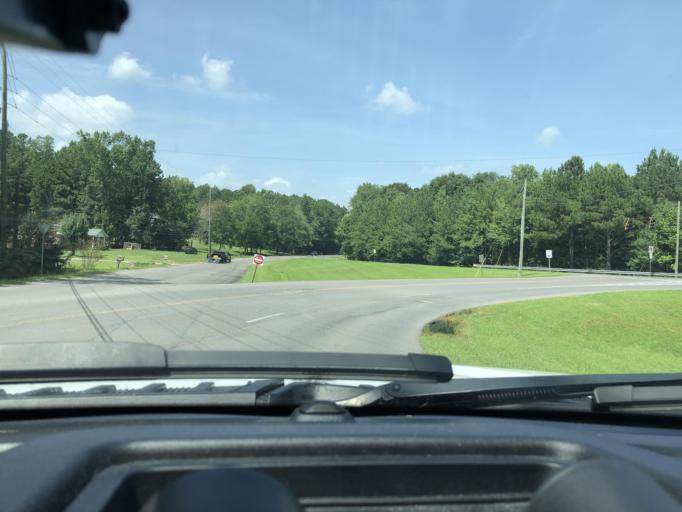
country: US
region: Georgia
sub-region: Whitfield County
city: Dalton
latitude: 34.7337
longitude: -84.9360
